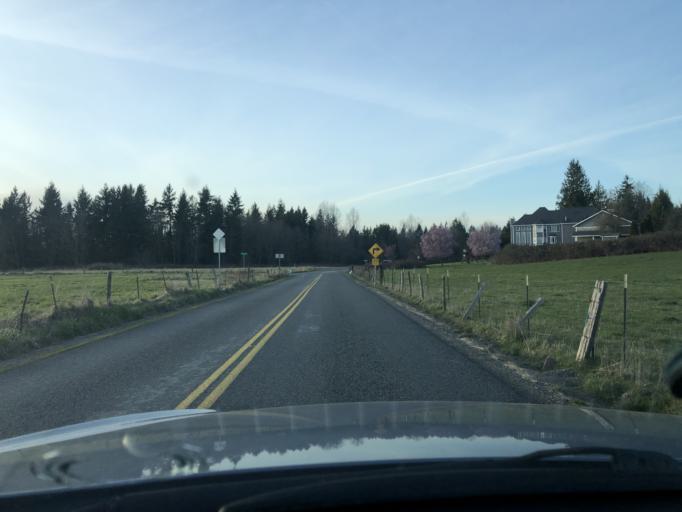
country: US
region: Washington
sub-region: Pierce County
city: Prairie Ridge
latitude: 47.2013
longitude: -122.1216
